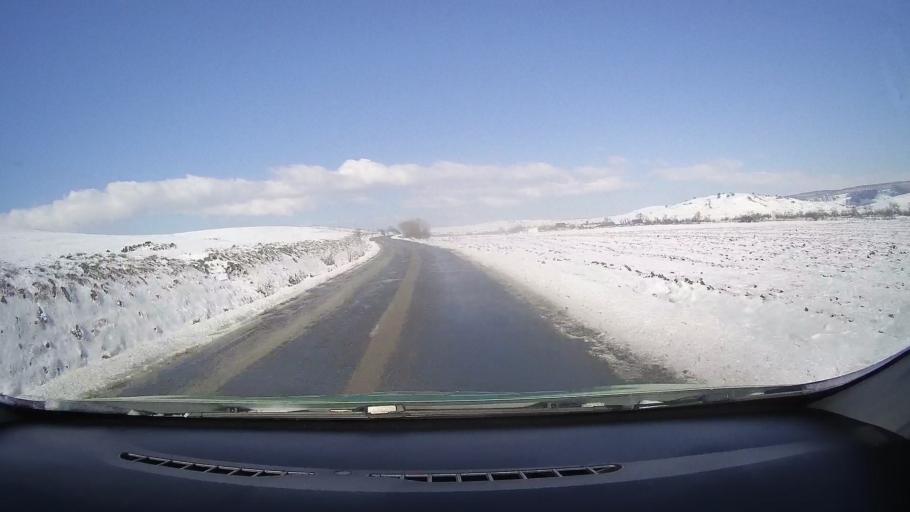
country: RO
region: Sibiu
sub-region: Comuna Rosia
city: Rosia
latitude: 45.8285
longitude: 24.3132
